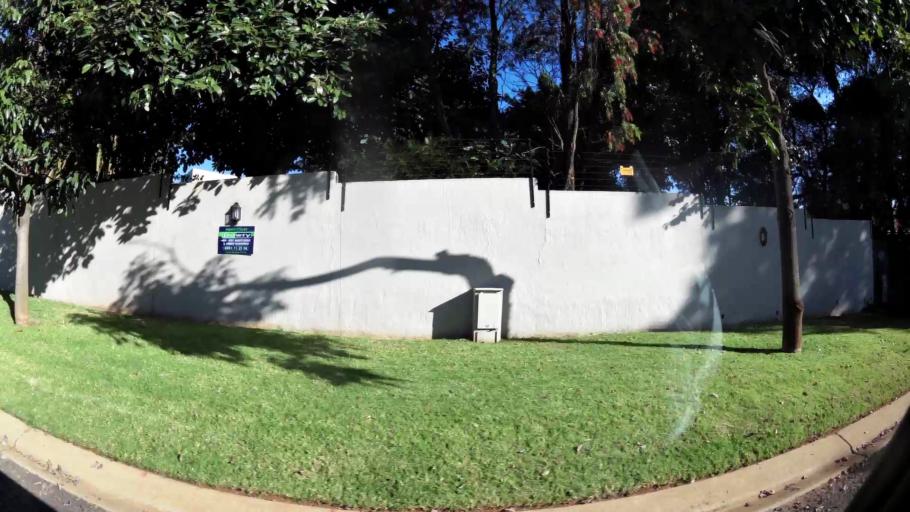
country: ZA
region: Gauteng
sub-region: City of Johannesburg Metropolitan Municipality
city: Roodepoort
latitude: -26.0904
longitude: 27.9500
